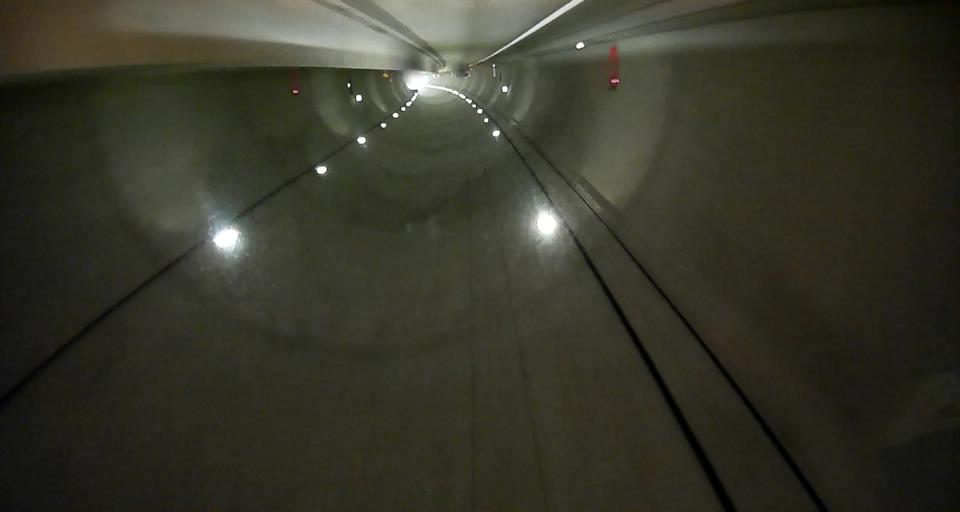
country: JP
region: Iwate
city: Yamada
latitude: 39.5328
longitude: 141.9197
